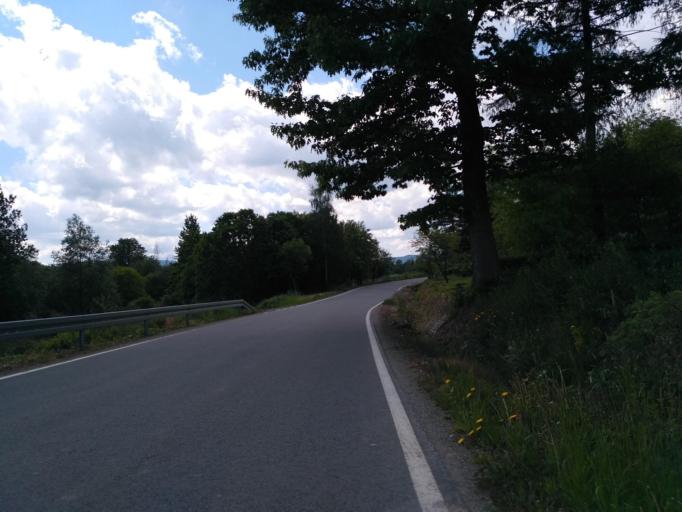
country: PL
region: Subcarpathian Voivodeship
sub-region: Powiat krosnienski
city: Dukla
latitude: 49.5931
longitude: 21.6994
